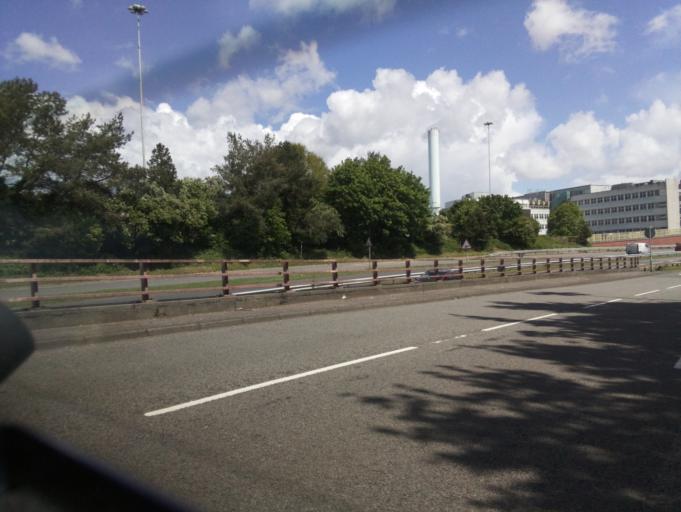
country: GB
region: Wales
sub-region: Cardiff
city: Cardiff
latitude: 51.5063
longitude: -3.1946
